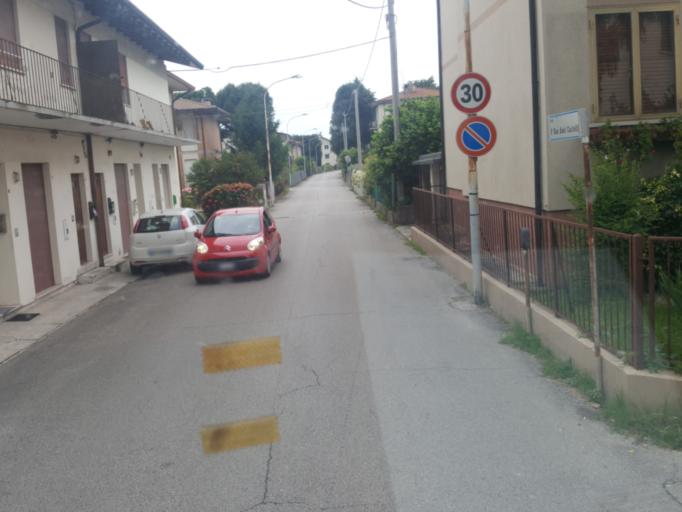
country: IT
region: Veneto
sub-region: Provincia di Vicenza
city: San Zeno-San Giuseppe
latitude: 45.7658
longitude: 11.7504
